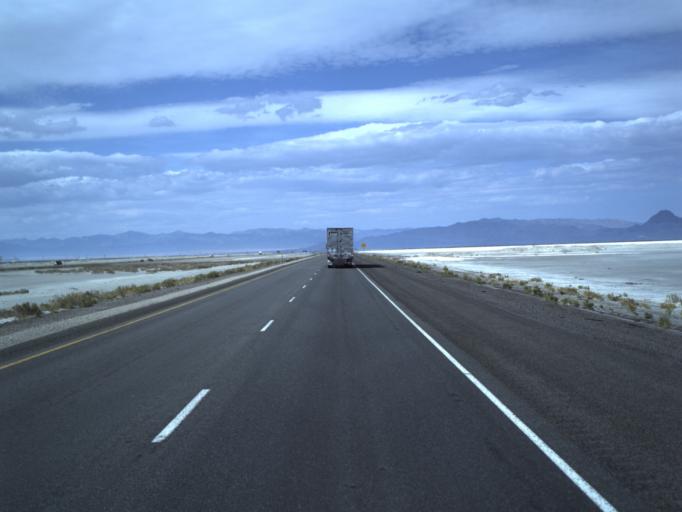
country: US
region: Utah
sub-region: Tooele County
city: Wendover
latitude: 40.7381
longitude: -113.7853
